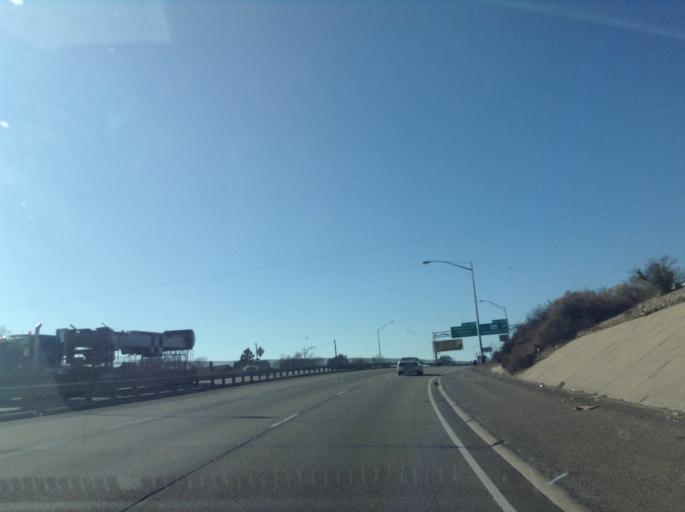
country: US
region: Texas
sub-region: Potter County
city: Amarillo
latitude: 35.1771
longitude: -101.8435
